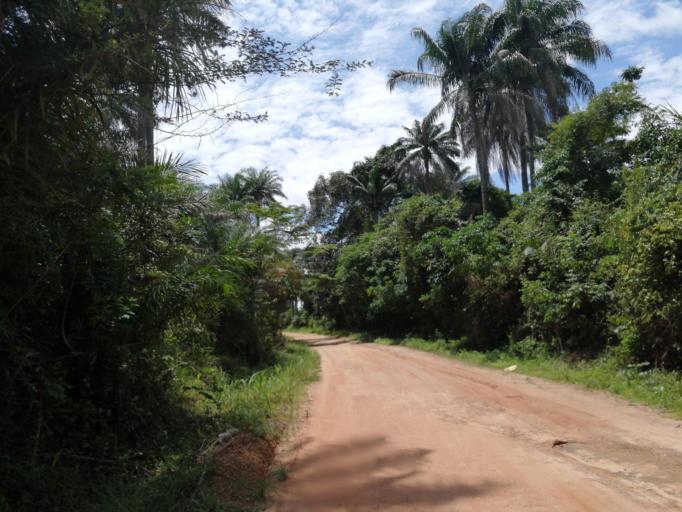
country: SL
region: Northern Province
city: Konakridee
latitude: 8.7527
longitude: -13.1436
